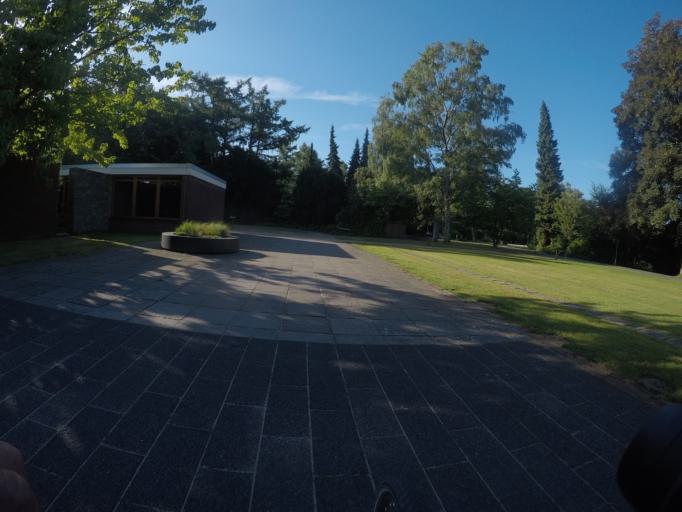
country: DE
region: Hamburg
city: Wandsbek
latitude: 53.5559
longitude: 10.1274
